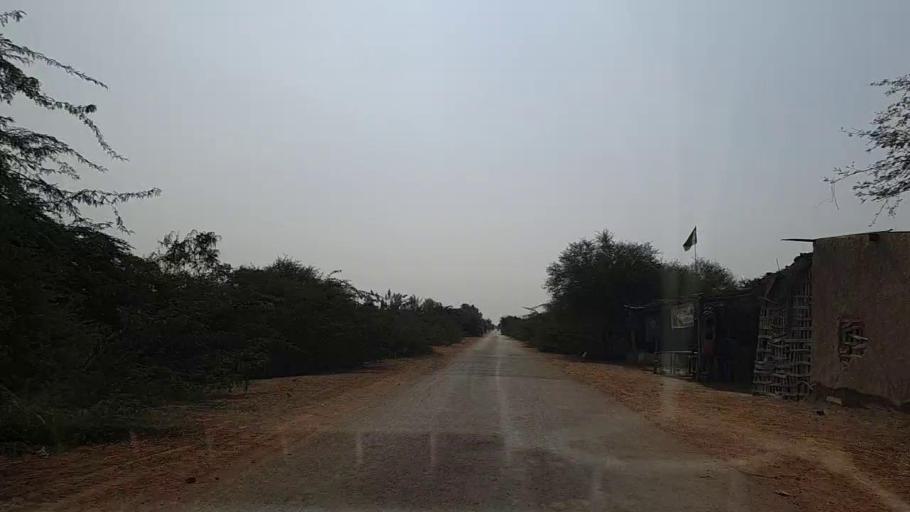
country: PK
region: Sindh
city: Chuhar Jamali
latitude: 24.2648
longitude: 67.9091
